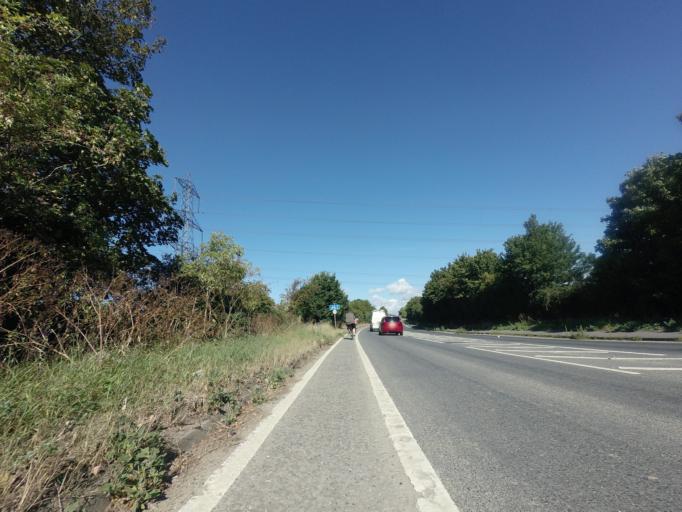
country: GB
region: England
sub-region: Kent
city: Gravesend
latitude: 51.4227
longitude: 0.4245
